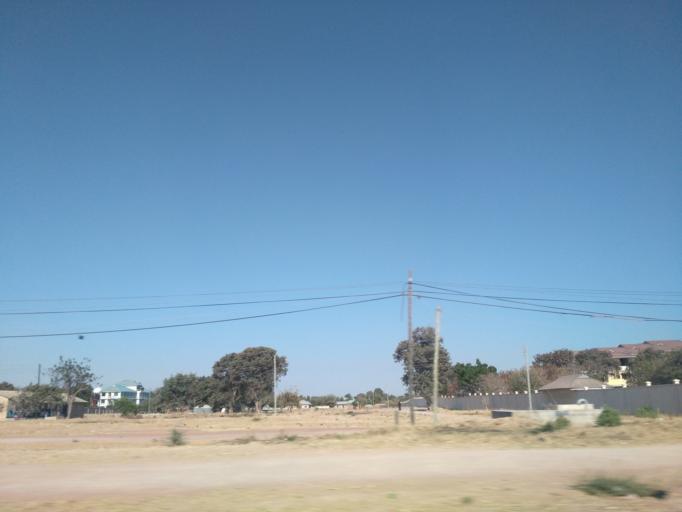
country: TZ
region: Dodoma
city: Dodoma
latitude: -6.1271
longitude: 35.7465
